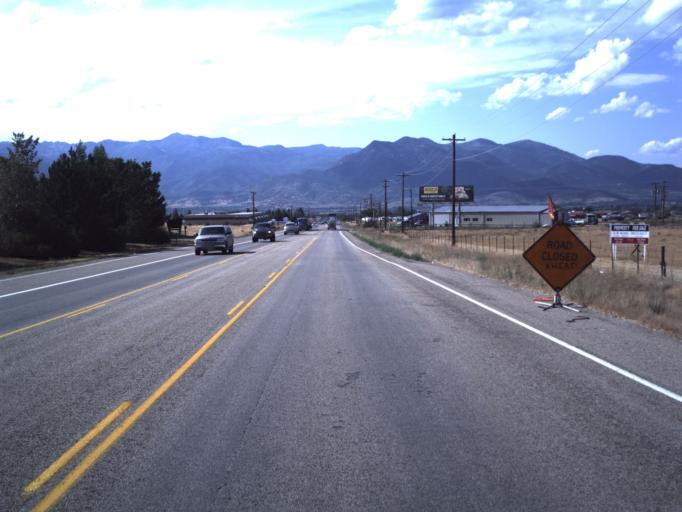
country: US
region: Utah
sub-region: Wasatch County
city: Heber
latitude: 40.4766
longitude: -111.3966
